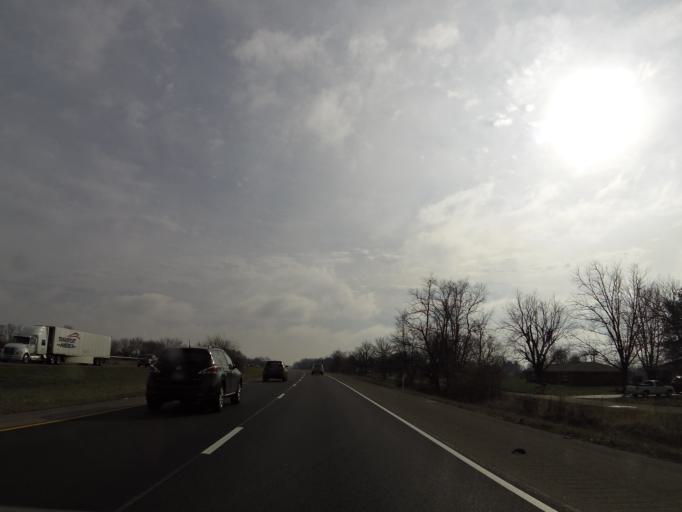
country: US
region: Indiana
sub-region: Shelby County
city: Shelbyville
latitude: 39.6041
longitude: -85.8516
